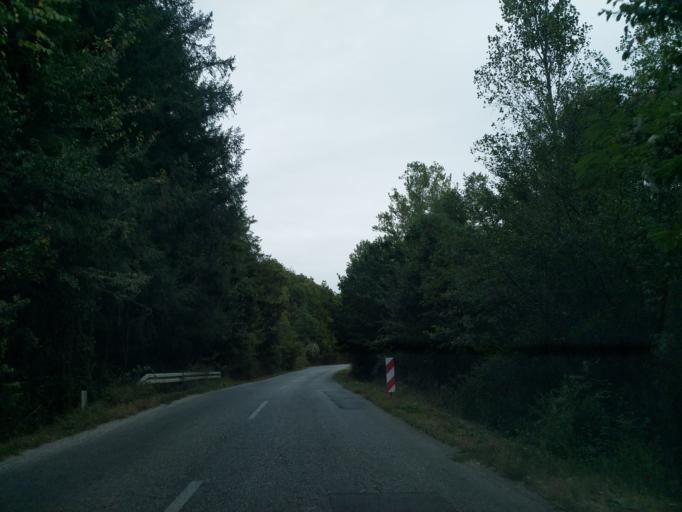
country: RS
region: Central Serbia
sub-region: Pomoravski Okrug
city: Jagodina
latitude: 44.0332
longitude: 21.1927
